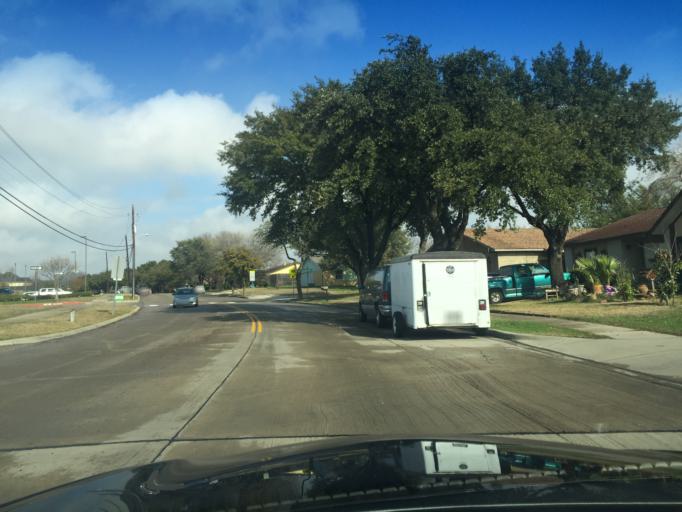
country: US
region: Texas
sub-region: Dallas County
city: Carrollton
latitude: 32.9940
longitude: -96.8801
